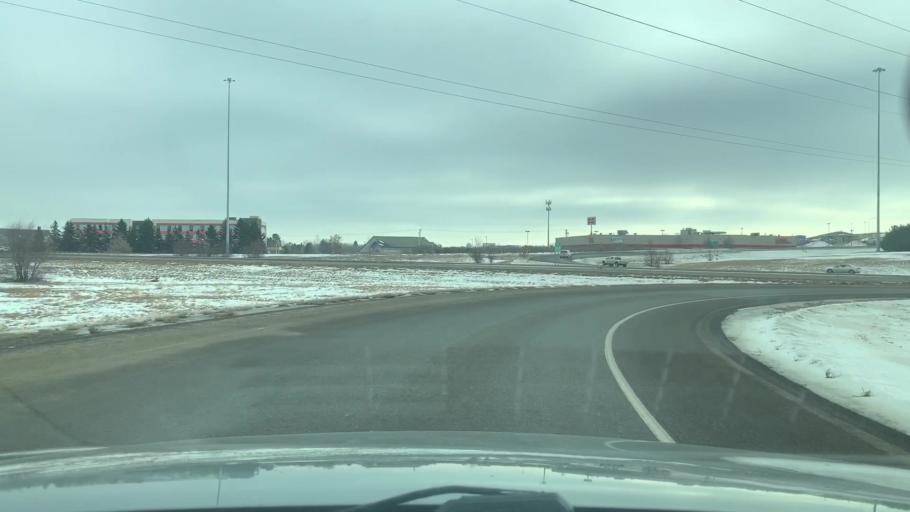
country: US
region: North Dakota
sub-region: Burleigh County
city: Bismarck
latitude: 46.8286
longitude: -100.8153
